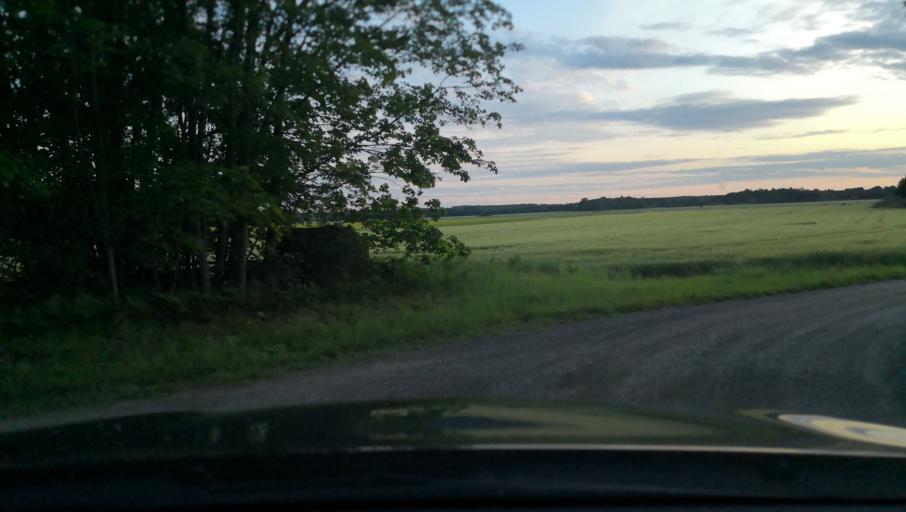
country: SE
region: Uppsala
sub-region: Osthammars Kommun
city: Bjorklinge
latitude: 60.0548
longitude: 17.6035
